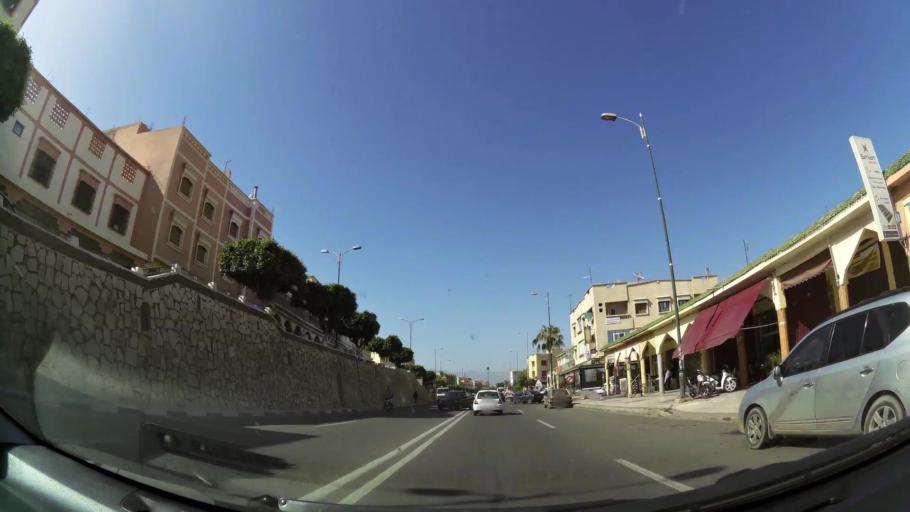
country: MA
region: Souss-Massa-Draa
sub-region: Inezgane-Ait Mellou
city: Inezgane
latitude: 30.3677
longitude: -9.5328
